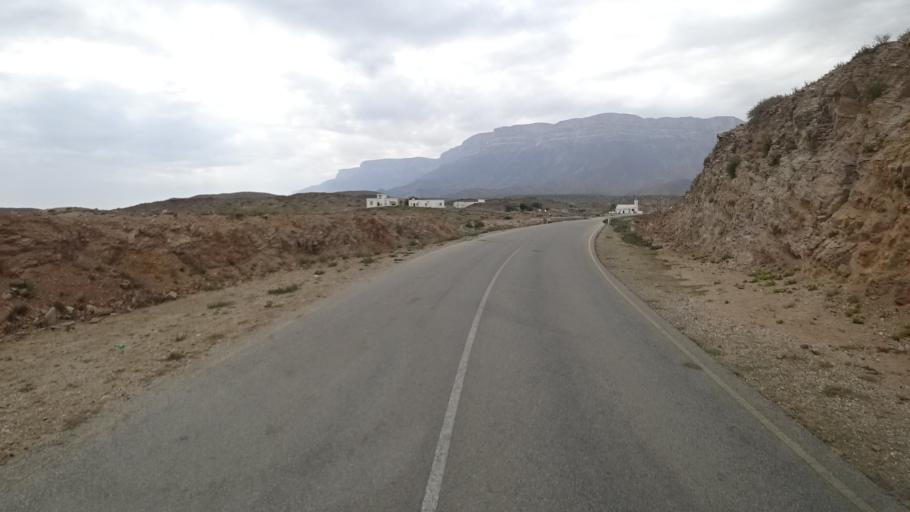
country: OM
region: Zufar
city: Salalah
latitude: 17.1622
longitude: 54.9855
